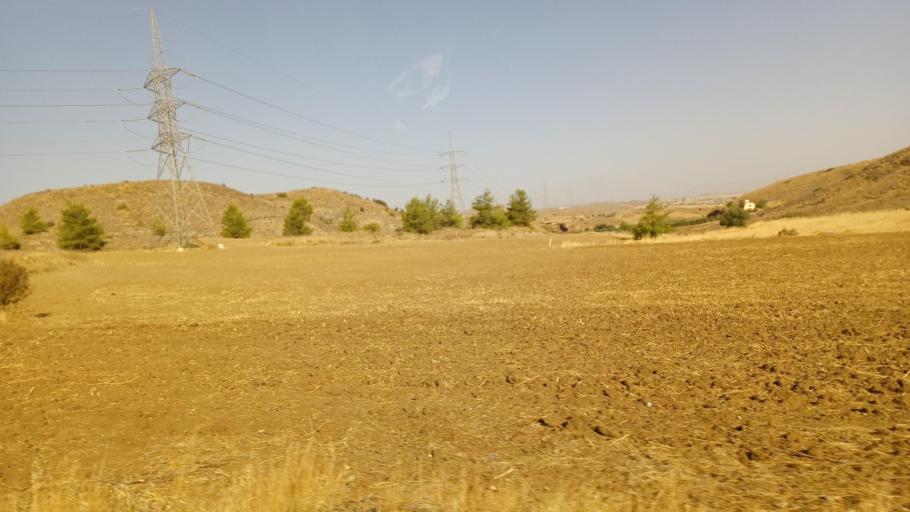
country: CY
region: Lefkosia
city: Alampra
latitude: 34.9818
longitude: 33.3484
